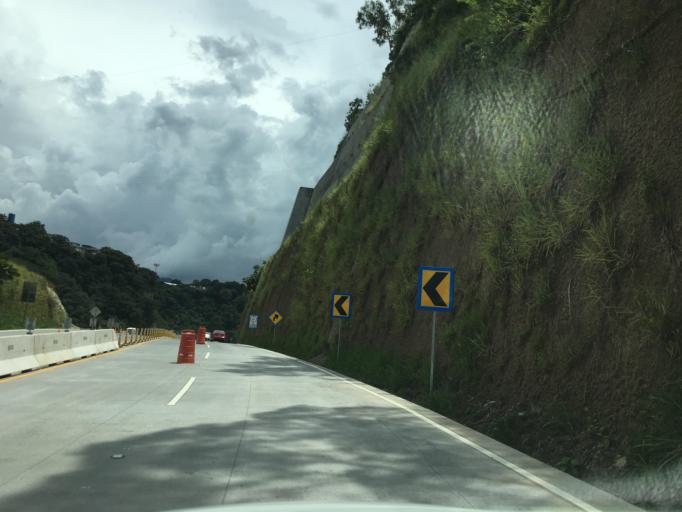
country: GT
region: Guatemala
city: Santa Catarina Pinula
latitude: 14.5512
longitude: -90.5325
